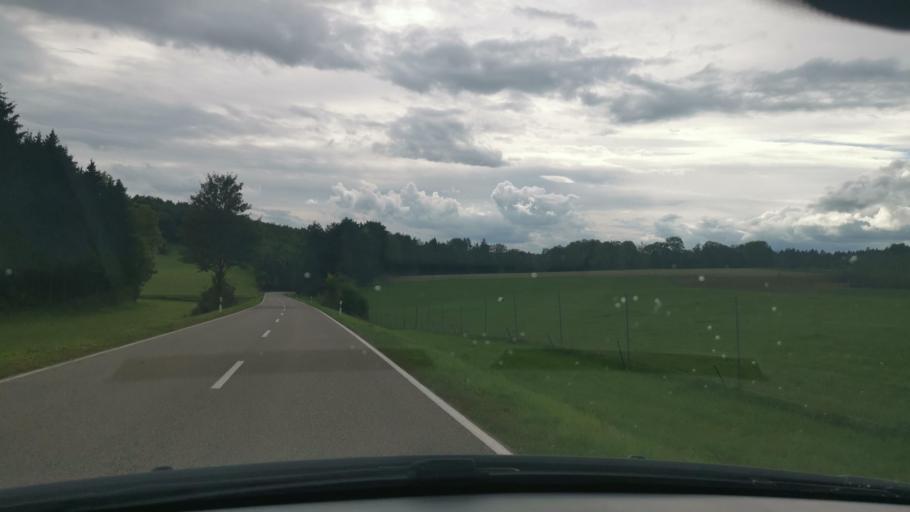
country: DE
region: Baden-Wuerttemberg
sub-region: Tuebingen Region
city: Hayingen
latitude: 48.3072
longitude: 9.5295
